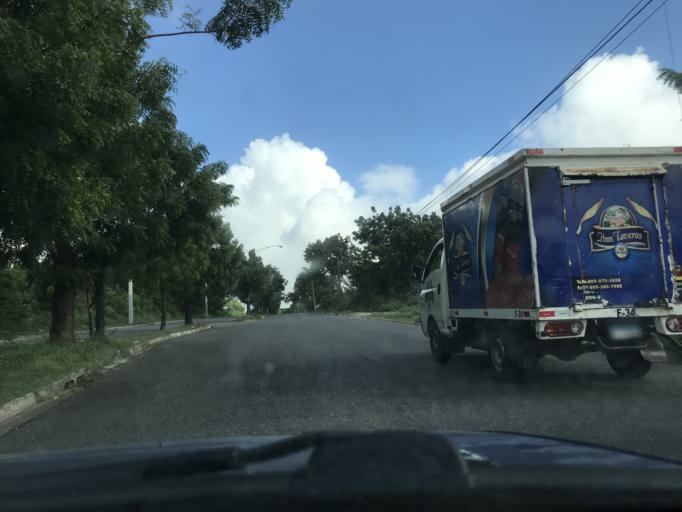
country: DO
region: Santiago
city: Santiago de los Caballeros
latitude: 19.4160
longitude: -70.7309
